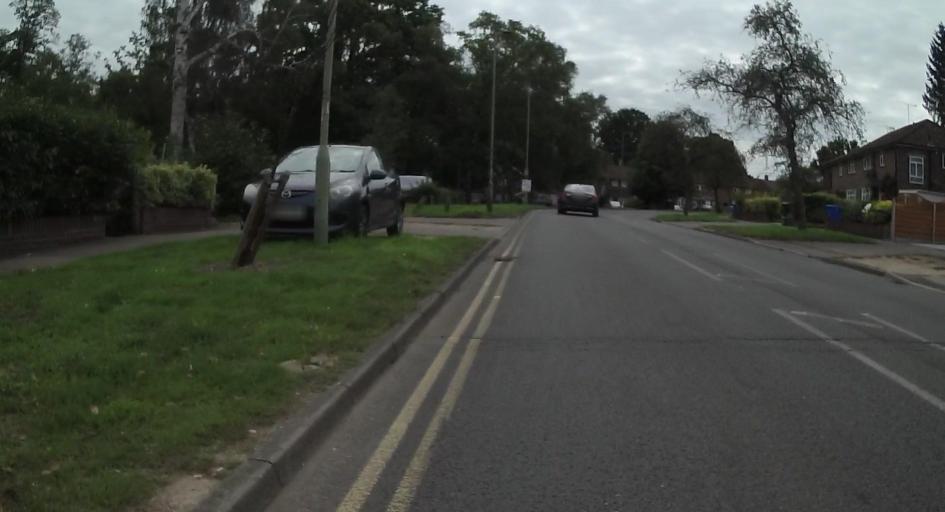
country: GB
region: England
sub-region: Surrey
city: West Byfleet
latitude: 51.3337
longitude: -0.5240
